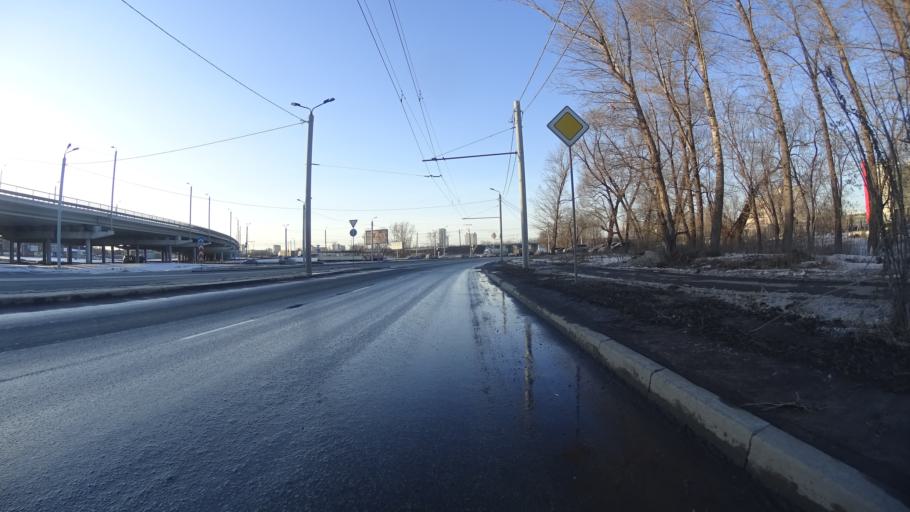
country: RU
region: Chelyabinsk
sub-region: Gorod Chelyabinsk
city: Chelyabinsk
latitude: 55.1503
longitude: 61.4437
